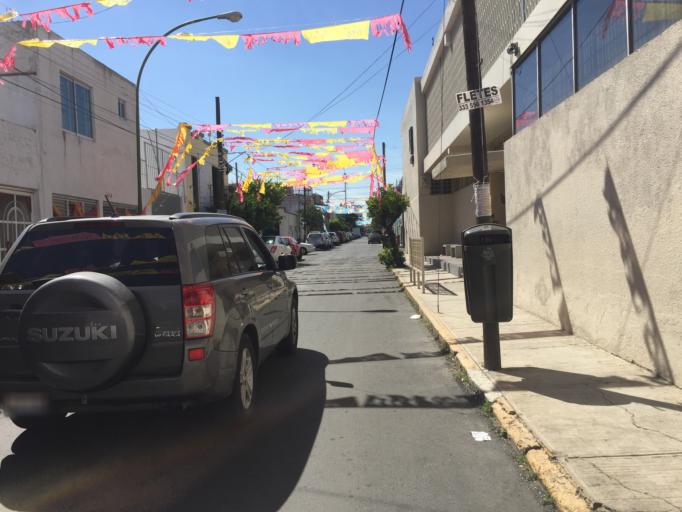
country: MX
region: Jalisco
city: Guadalajara
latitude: 20.6870
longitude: -103.3654
